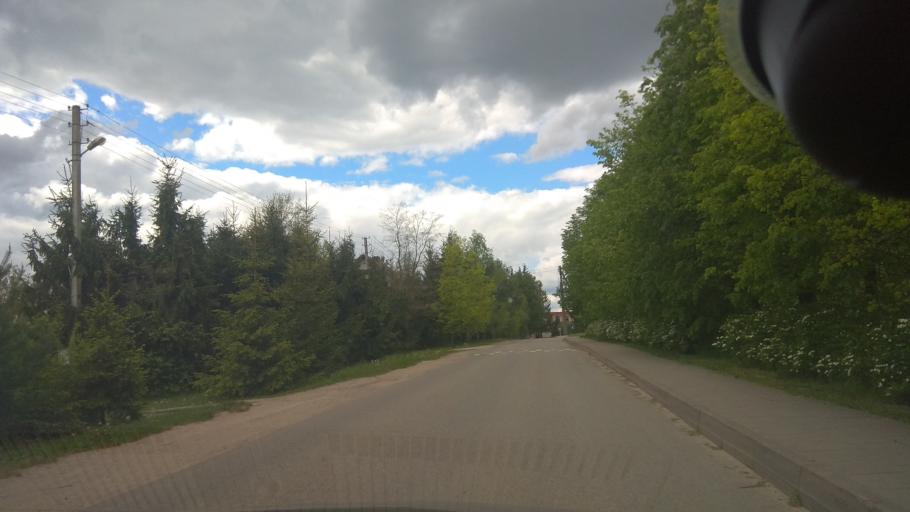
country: LT
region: Vilnius County
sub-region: Vilnius
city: Fabijoniskes
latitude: 54.8044
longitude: 25.2606
